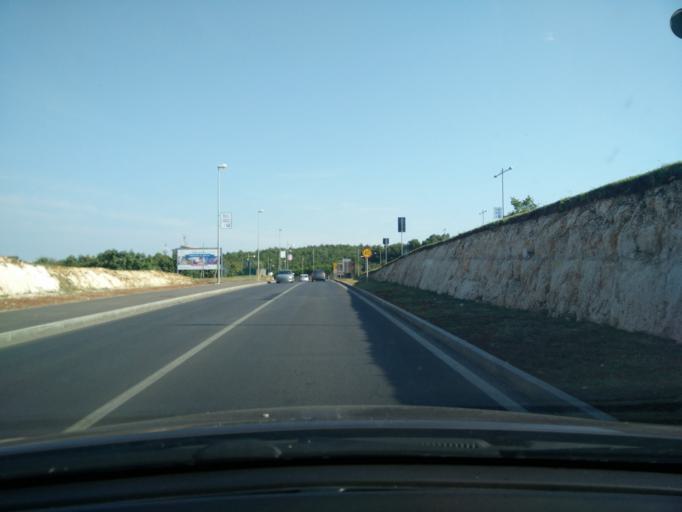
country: HR
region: Istarska
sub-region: Grad Porec
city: Porec
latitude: 45.2207
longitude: 13.6057
